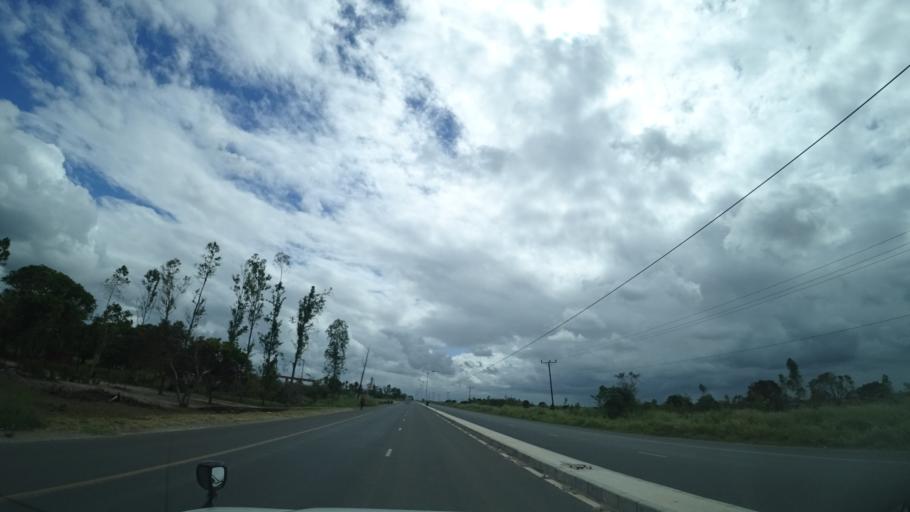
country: MZ
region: Sofala
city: Dondo
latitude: -19.5883
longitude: 34.7366
